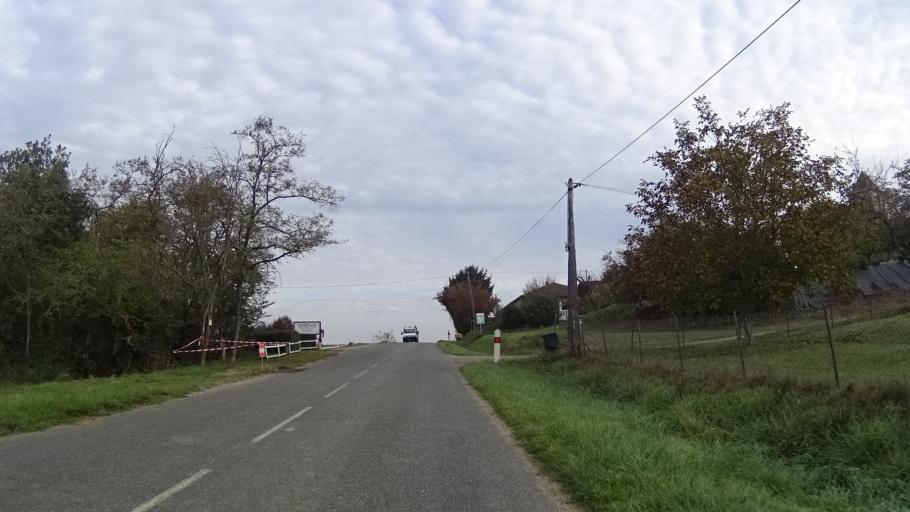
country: FR
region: Aquitaine
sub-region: Departement du Lot-et-Garonne
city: Laplume
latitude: 44.1059
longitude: 0.5715
